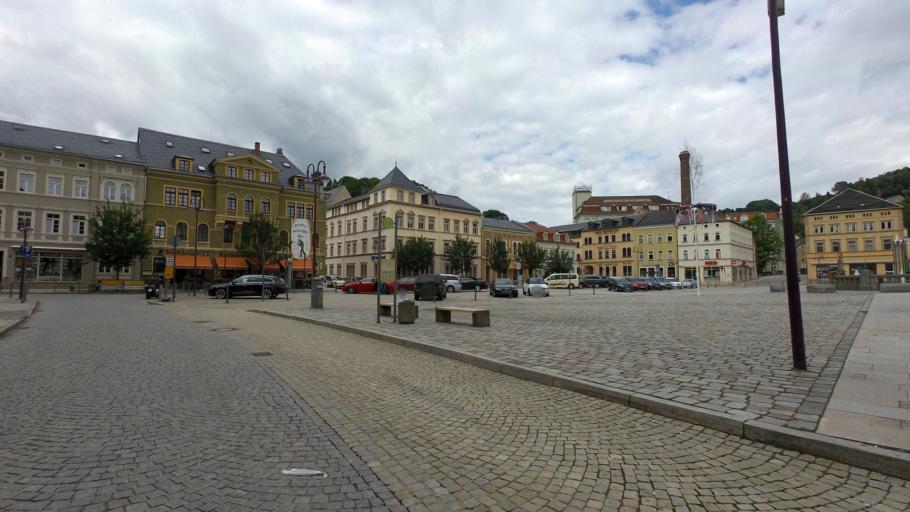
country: DE
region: Saxony
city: Sebnitz
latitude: 50.9725
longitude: 14.2712
